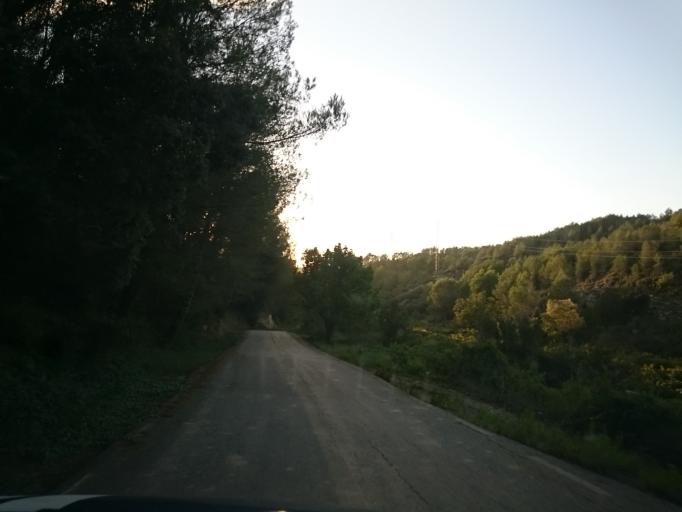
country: ES
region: Catalonia
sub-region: Provincia de Barcelona
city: Olivella
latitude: 41.3118
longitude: 1.8132
